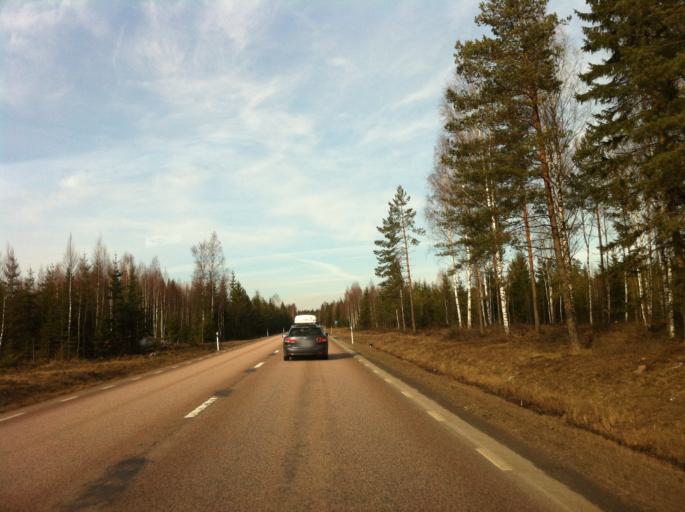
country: SE
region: Vaermland
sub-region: Kristinehamns Kommun
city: Bjorneborg
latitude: 59.1845
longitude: 14.1795
